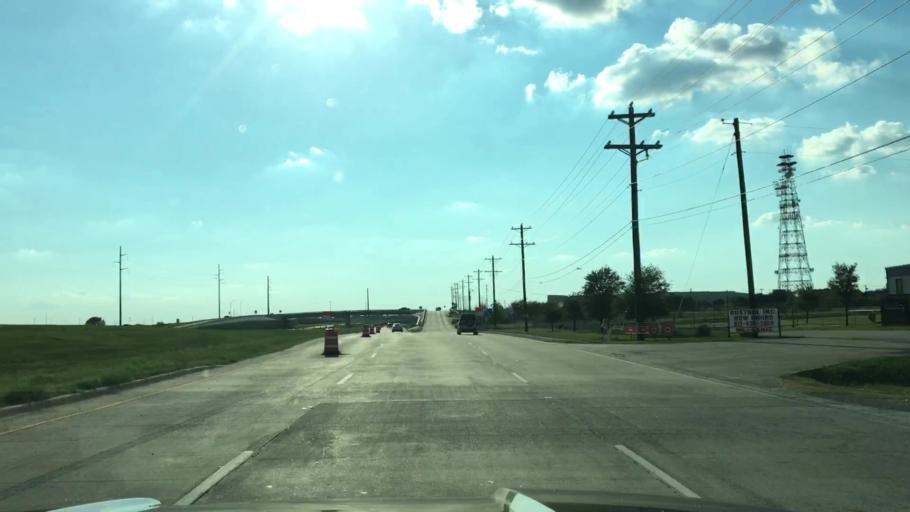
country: US
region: Texas
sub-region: Denton County
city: Justin
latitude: 33.0271
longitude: -97.2955
